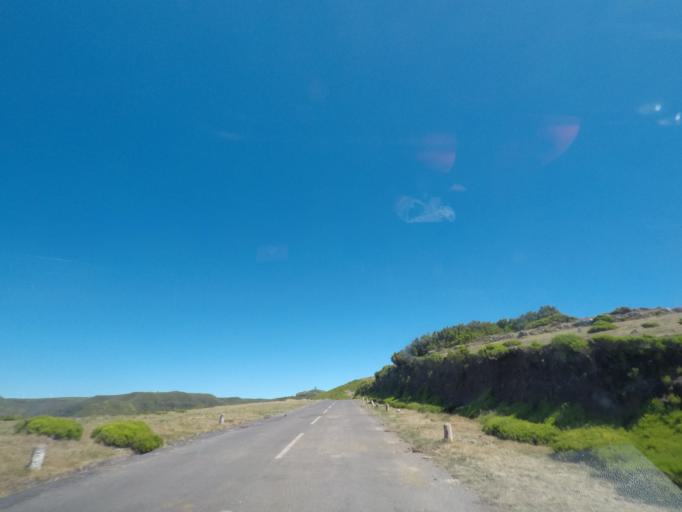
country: PT
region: Madeira
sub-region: Calheta
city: Arco da Calheta
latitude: 32.7635
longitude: -17.1440
